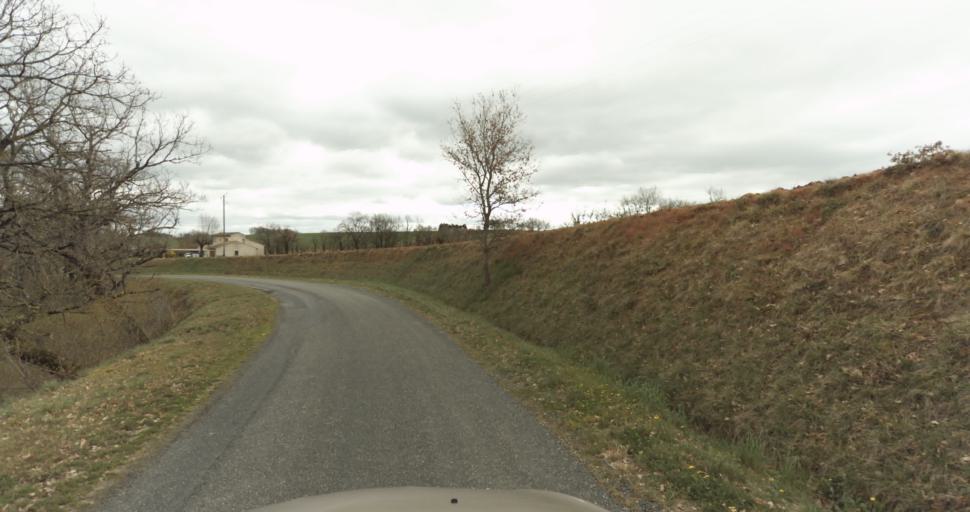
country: FR
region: Midi-Pyrenees
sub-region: Departement du Tarn
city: Puygouzon
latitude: 43.8699
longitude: 2.1697
